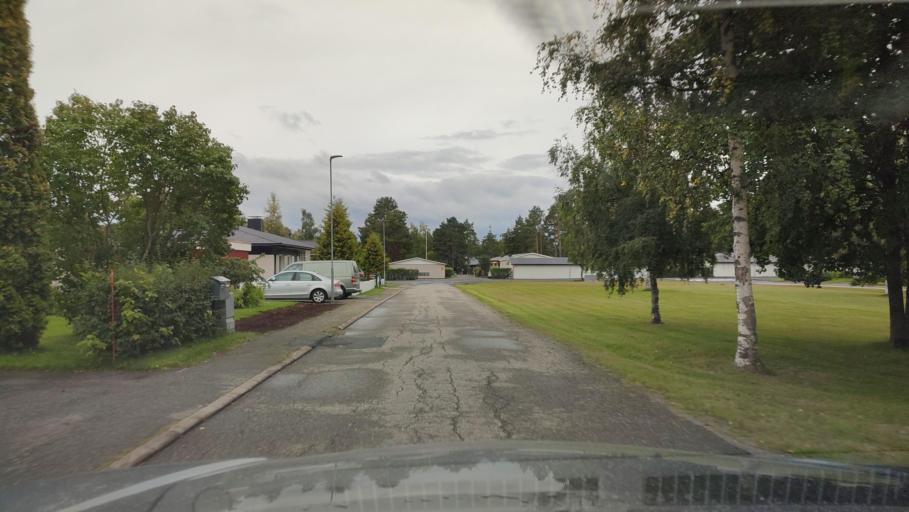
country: FI
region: Ostrobothnia
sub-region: Sydosterbotten
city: Kristinestad
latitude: 62.2825
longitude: 21.3597
